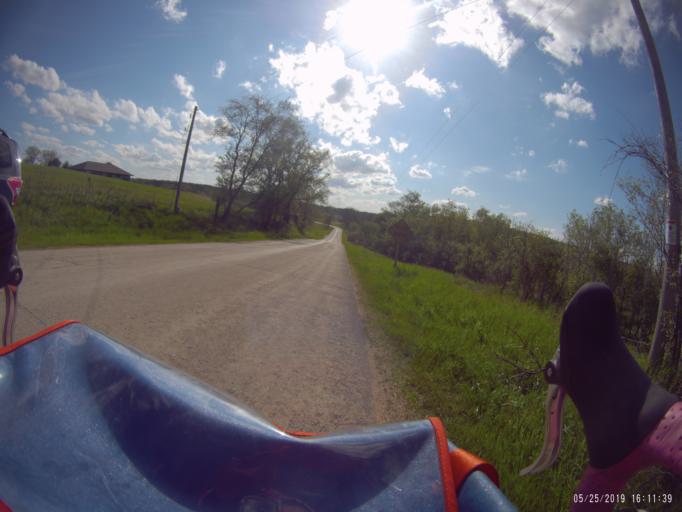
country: US
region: Wisconsin
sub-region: Dane County
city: Mount Horeb
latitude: 42.9628
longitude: -89.6683
